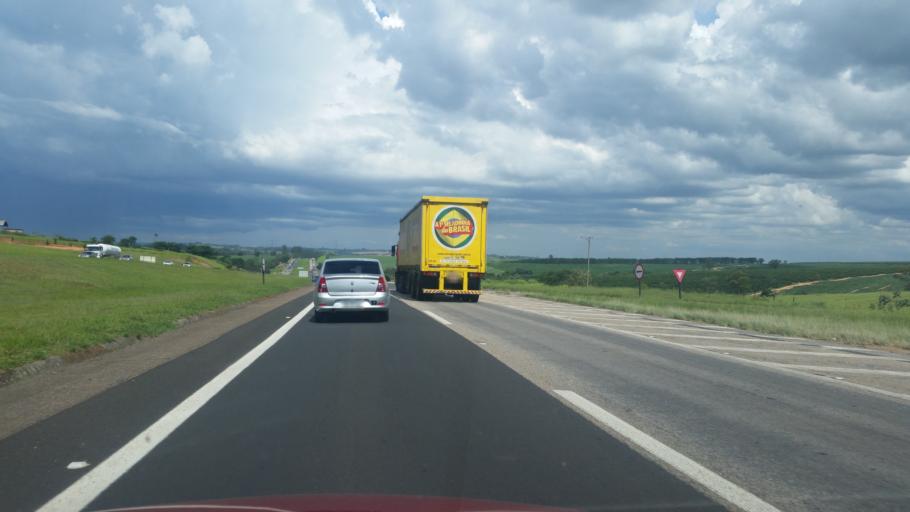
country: BR
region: Sao Paulo
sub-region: Tatui
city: Tatui
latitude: -23.2833
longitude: -47.8044
